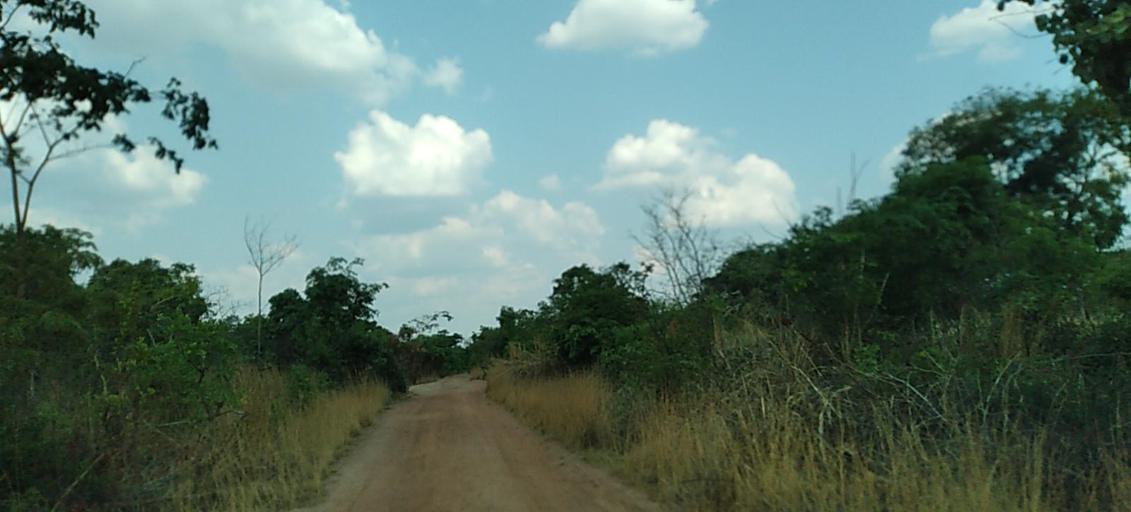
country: ZM
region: Copperbelt
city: Luanshya
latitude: -13.1561
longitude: 28.3264
